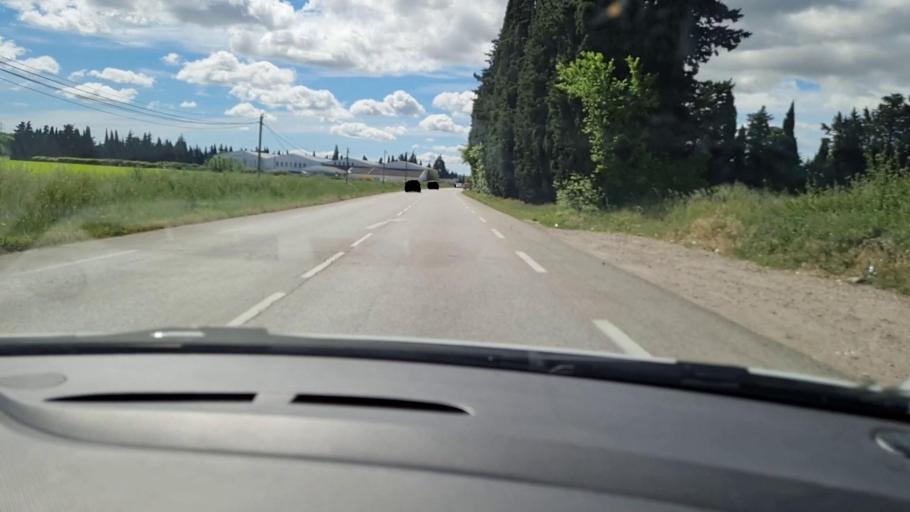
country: FR
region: Languedoc-Roussillon
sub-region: Departement du Gard
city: Milhaud
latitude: 43.8029
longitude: 4.3389
